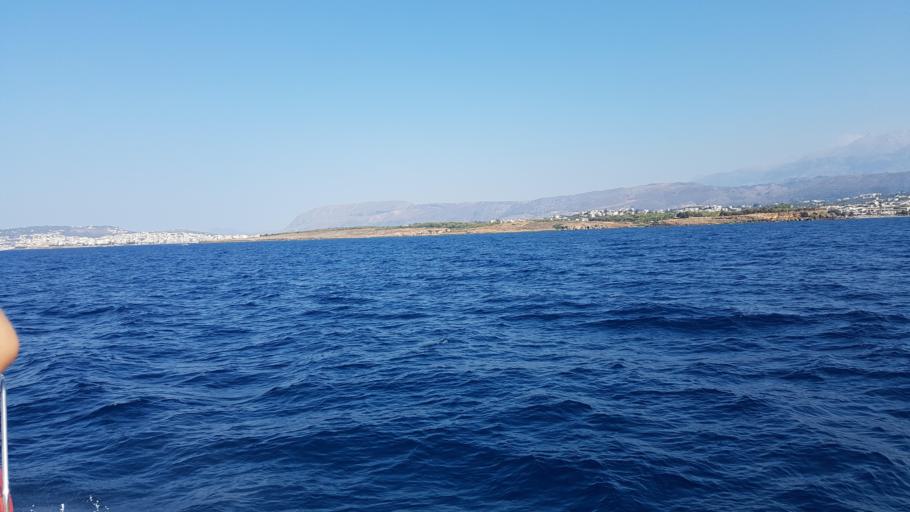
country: GR
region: Crete
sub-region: Nomos Chanias
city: Daratsos
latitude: 35.5230
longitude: 23.9718
